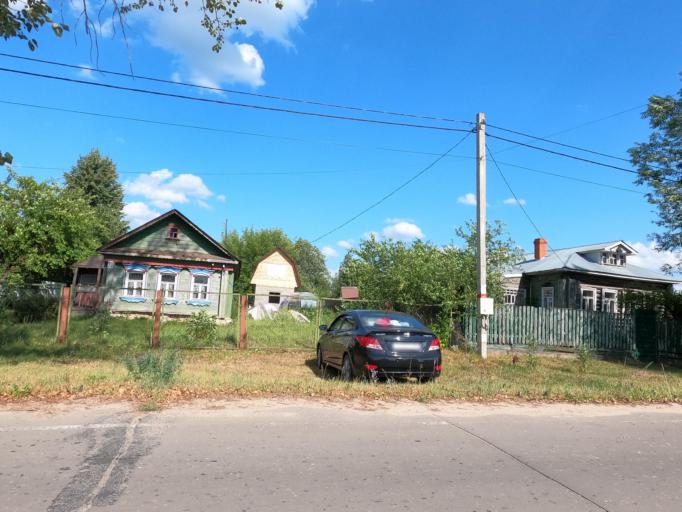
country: RU
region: Moskovskaya
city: Peski
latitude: 55.2270
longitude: 38.7507
